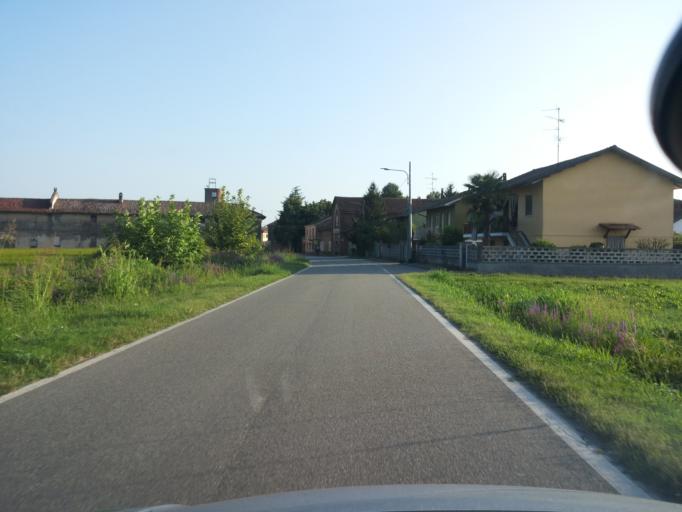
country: IT
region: Piedmont
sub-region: Provincia di Vercelli
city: Sali Vercellese
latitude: 45.3112
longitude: 8.3297
